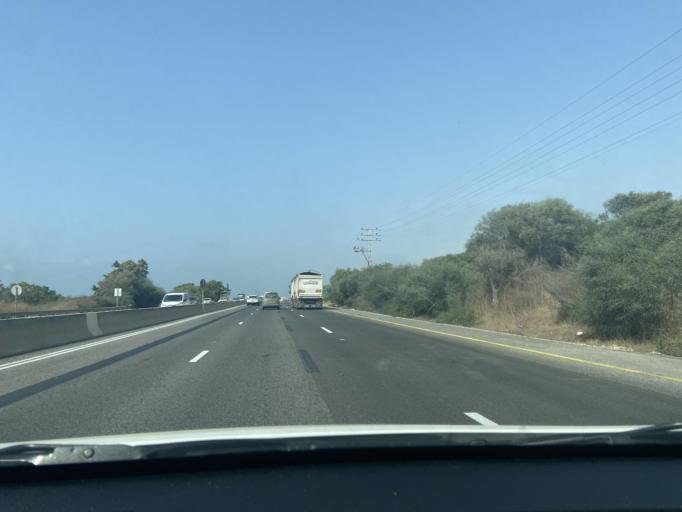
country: IL
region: Northern District
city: El Mazra`a
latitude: 32.9680
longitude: 35.0932
